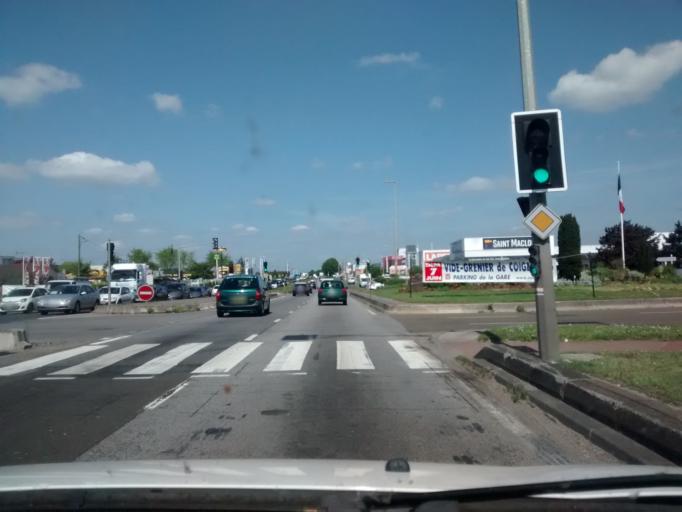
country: FR
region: Ile-de-France
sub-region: Departement des Yvelines
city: Coignieres
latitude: 48.7483
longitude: 1.9248
